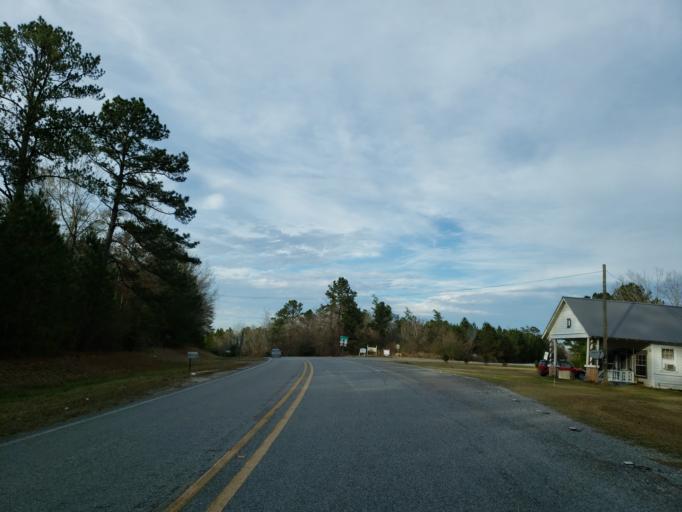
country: US
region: Mississippi
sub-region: Wayne County
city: Waynesboro
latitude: 31.8433
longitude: -88.6866
